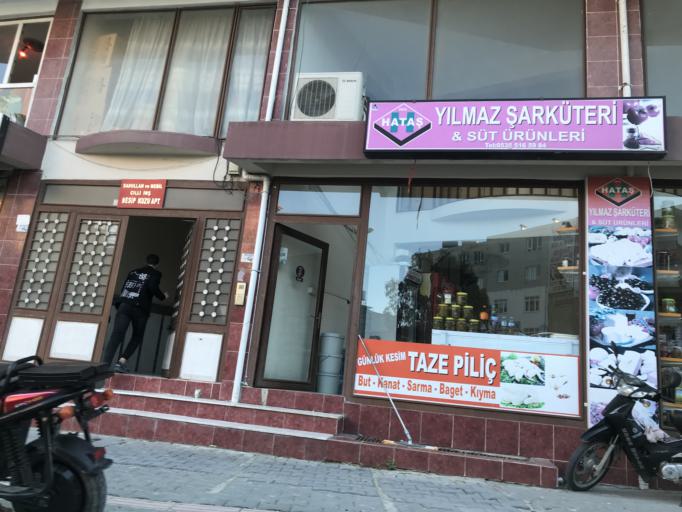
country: TR
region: Hatay
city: Samandag
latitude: 36.0830
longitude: 35.9894
